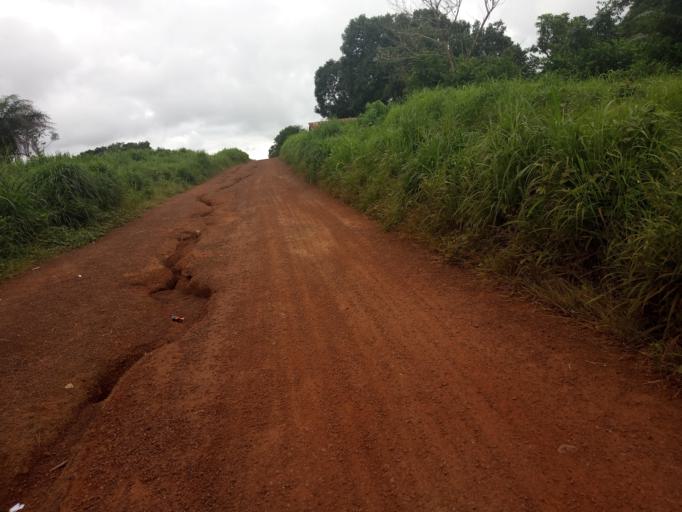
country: SL
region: Northern Province
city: Kamakwie
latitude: 9.5028
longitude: -12.2556
